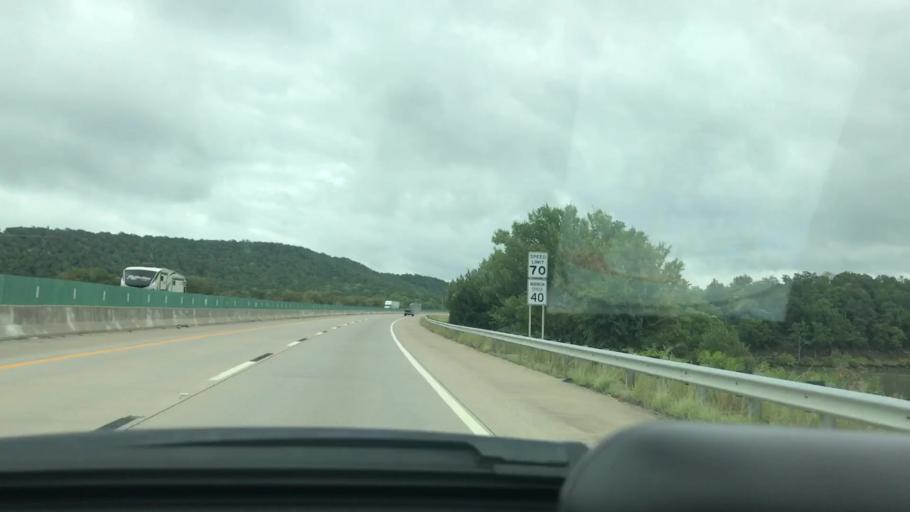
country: US
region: Oklahoma
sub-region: Pittsburg County
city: Krebs
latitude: 35.1096
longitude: -95.6929
